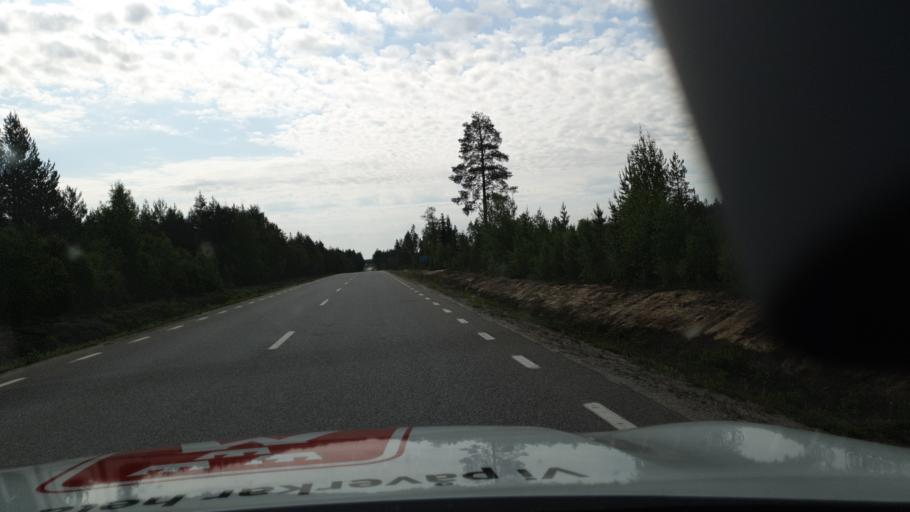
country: SE
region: Vaesterbotten
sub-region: Norsjo Kommun
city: Norsjoe
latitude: 64.5524
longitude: 19.3264
